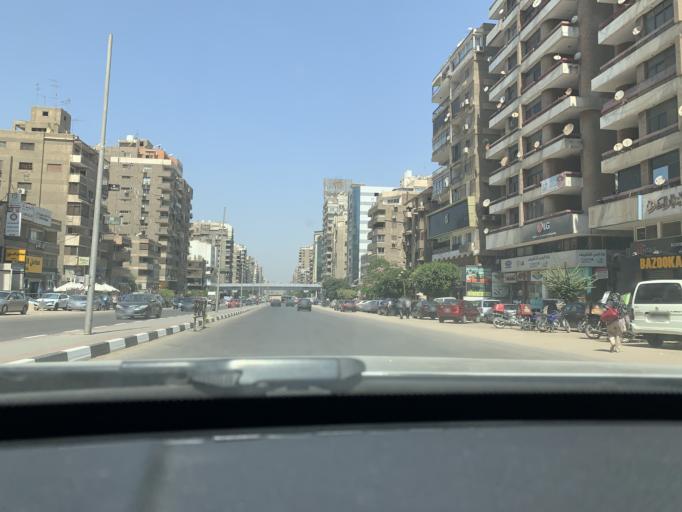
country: EG
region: Muhafazat al Qahirah
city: Cairo
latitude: 30.0520
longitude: 31.3466
